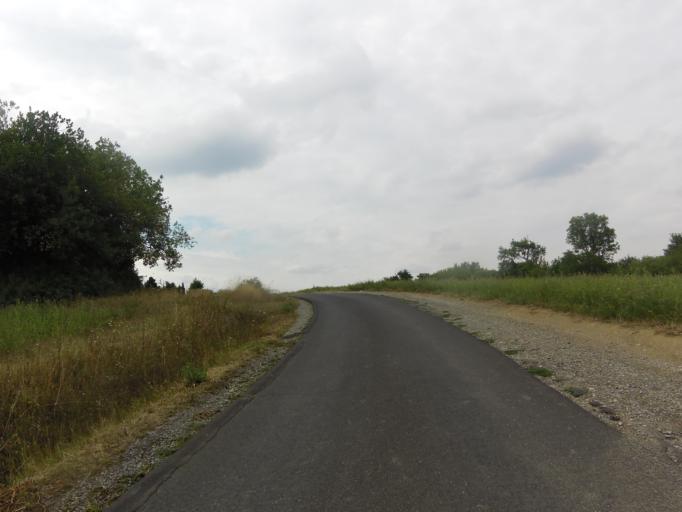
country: DE
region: Bavaria
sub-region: Regierungsbezirk Unterfranken
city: Wuerzburg
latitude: 49.7695
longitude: 9.8767
